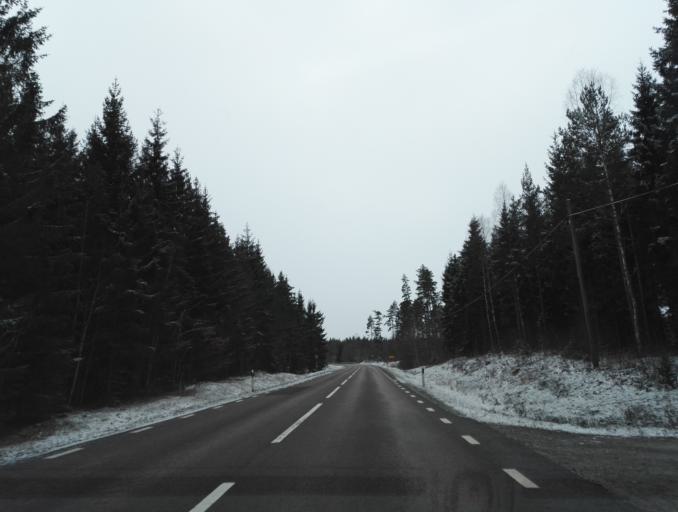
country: SE
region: Kalmar
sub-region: Hultsfreds Kommun
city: Virserum
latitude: 57.1949
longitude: 15.5092
